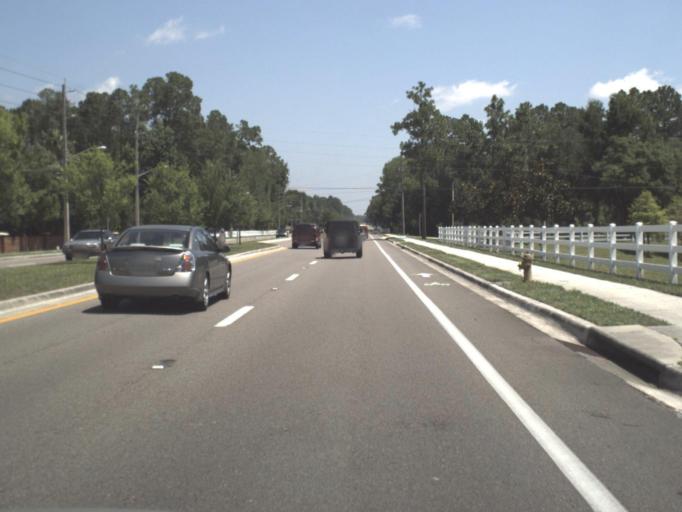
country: US
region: Florida
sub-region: Saint Johns County
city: Fruit Cove
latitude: 30.0965
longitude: -81.6276
